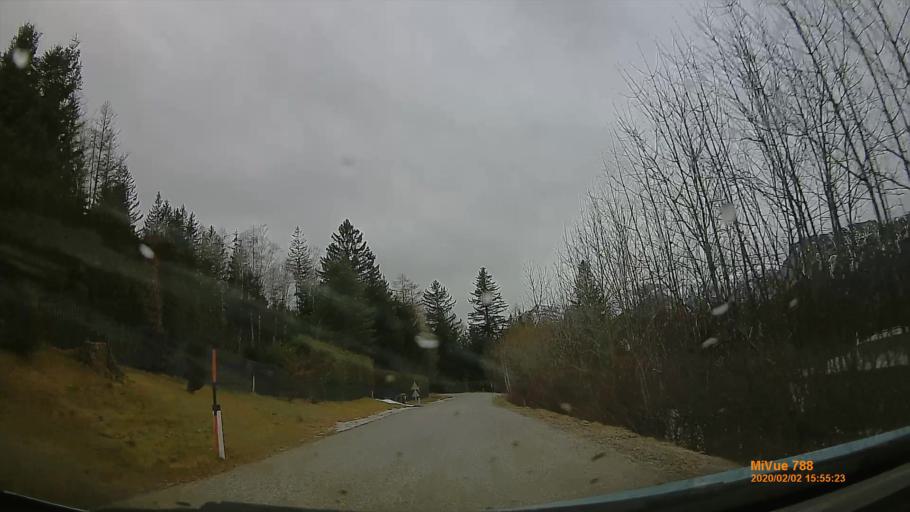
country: AT
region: Lower Austria
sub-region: Politischer Bezirk Neunkirchen
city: Semmering
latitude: 47.6703
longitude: 15.7875
